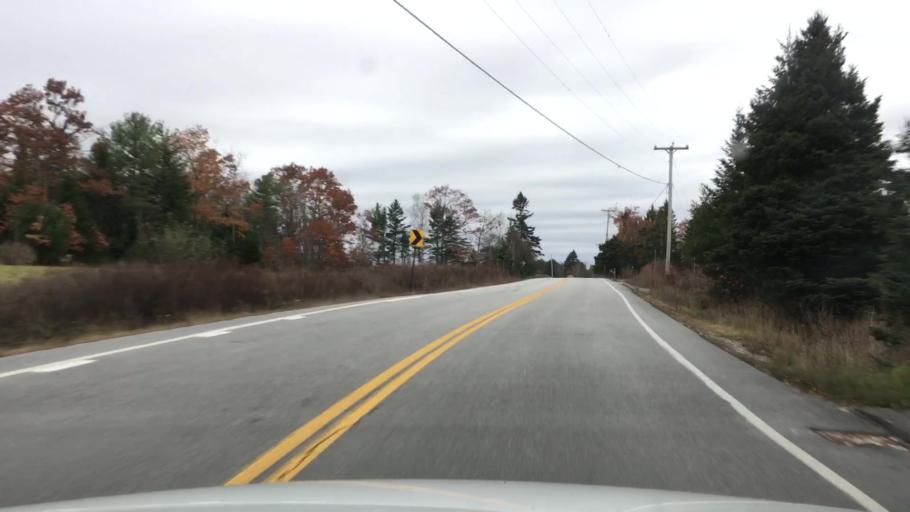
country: US
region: Maine
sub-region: Hancock County
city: Orland
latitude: 44.5311
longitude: -68.6751
